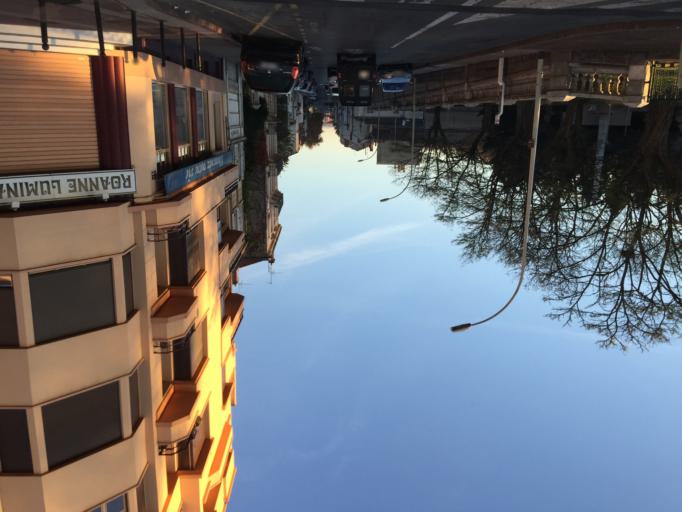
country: FR
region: Rhone-Alpes
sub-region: Departement de la Loire
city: Roanne
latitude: 46.0335
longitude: 4.0775
